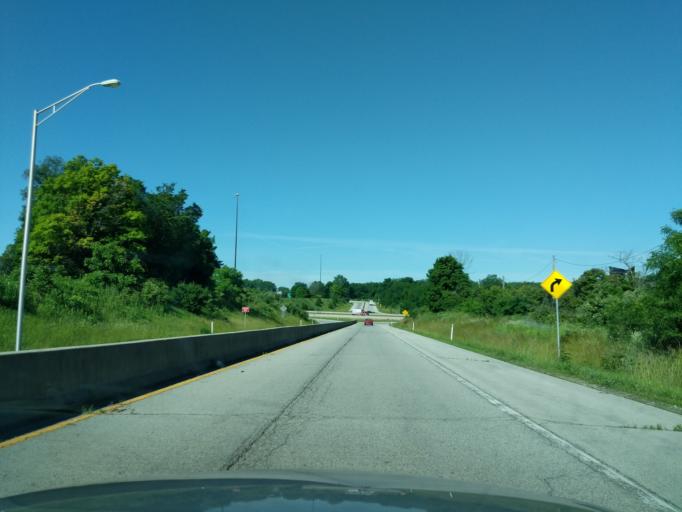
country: US
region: Indiana
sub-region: Delaware County
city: Daleville
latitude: 40.1200
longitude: -85.5662
